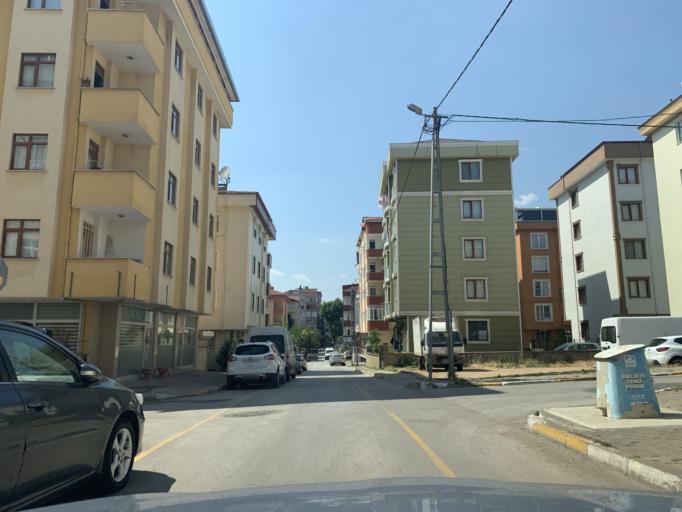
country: TR
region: Istanbul
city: Pendik
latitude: 40.8586
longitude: 29.2784
